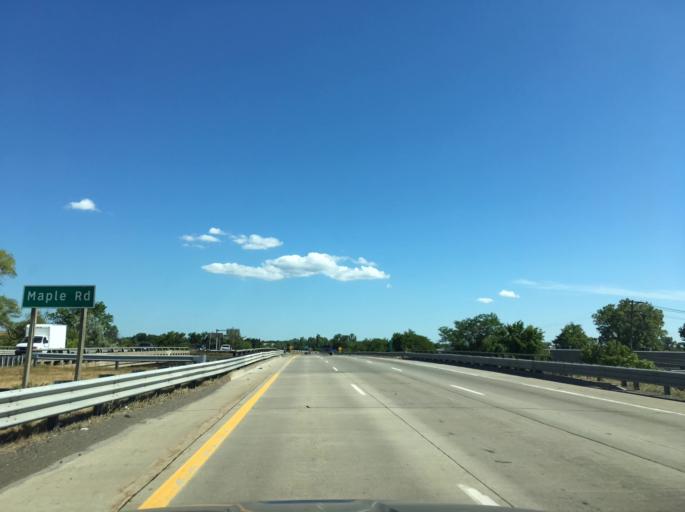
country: US
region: Michigan
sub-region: Oakland County
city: Clawson
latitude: 42.5485
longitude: -83.1166
